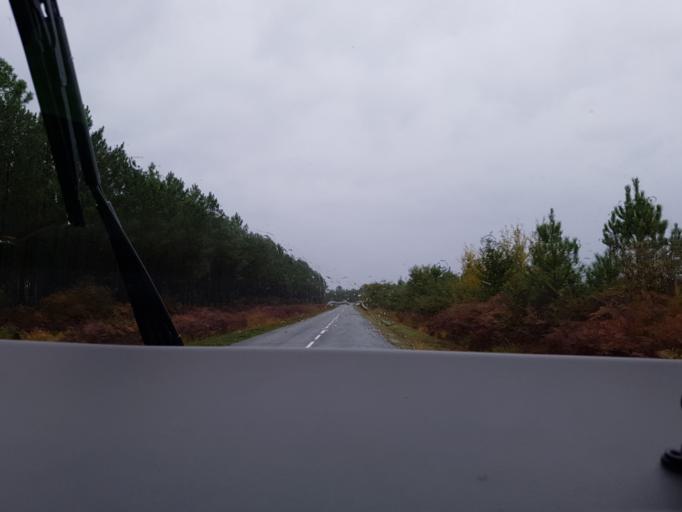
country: FR
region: Aquitaine
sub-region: Departement des Landes
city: Pissos
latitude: 44.3768
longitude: -0.6518
